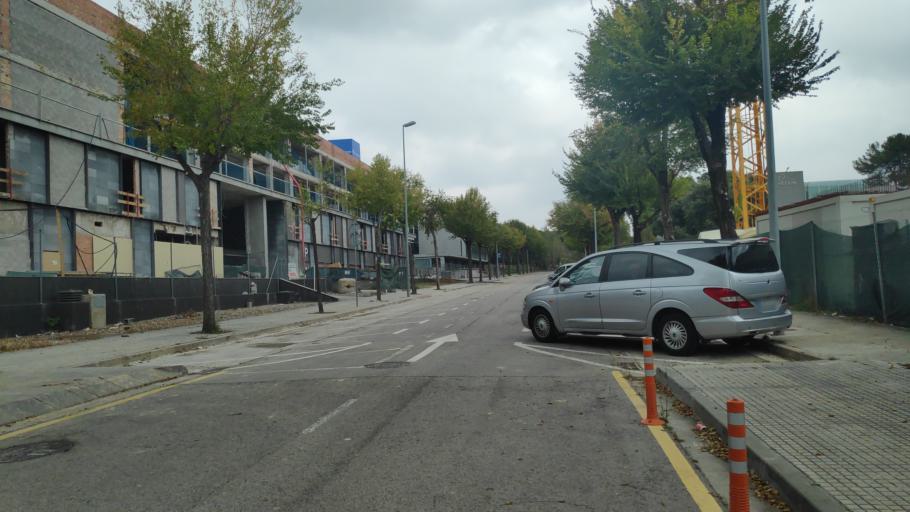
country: ES
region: Catalonia
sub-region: Provincia de Barcelona
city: Sant Cugat del Valles
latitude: 41.4805
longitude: 2.0625
